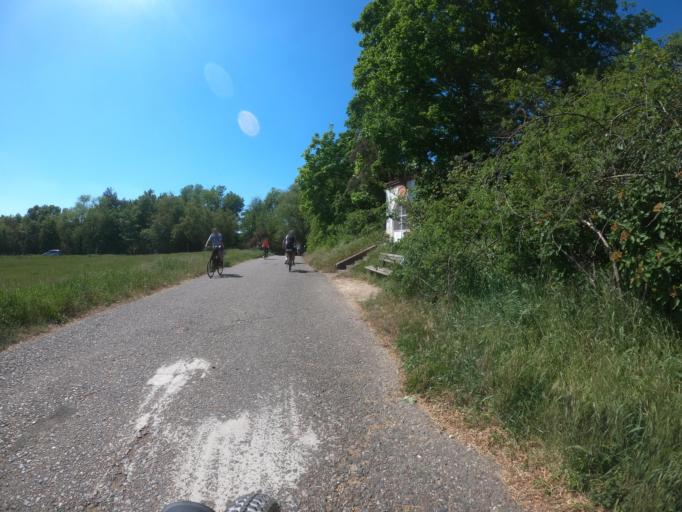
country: DE
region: Hesse
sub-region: Regierungsbezirk Darmstadt
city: Russelsheim
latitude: 50.0048
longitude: 8.4035
